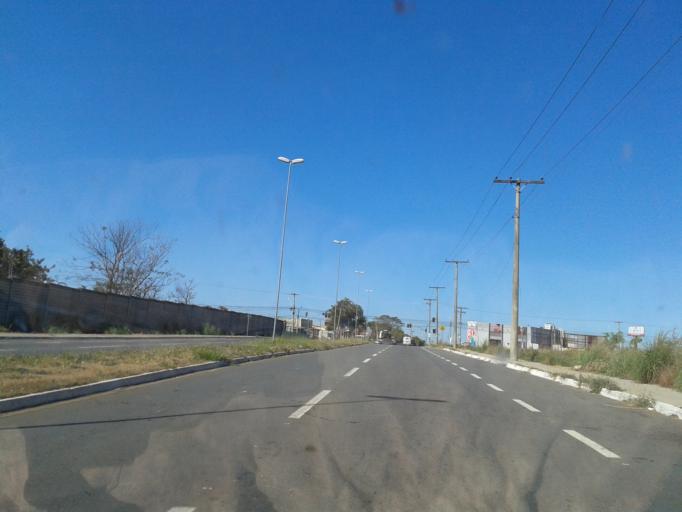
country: BR
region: Goias
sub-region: Goiania
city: Goiania
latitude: -16.7487
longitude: -49.3109
